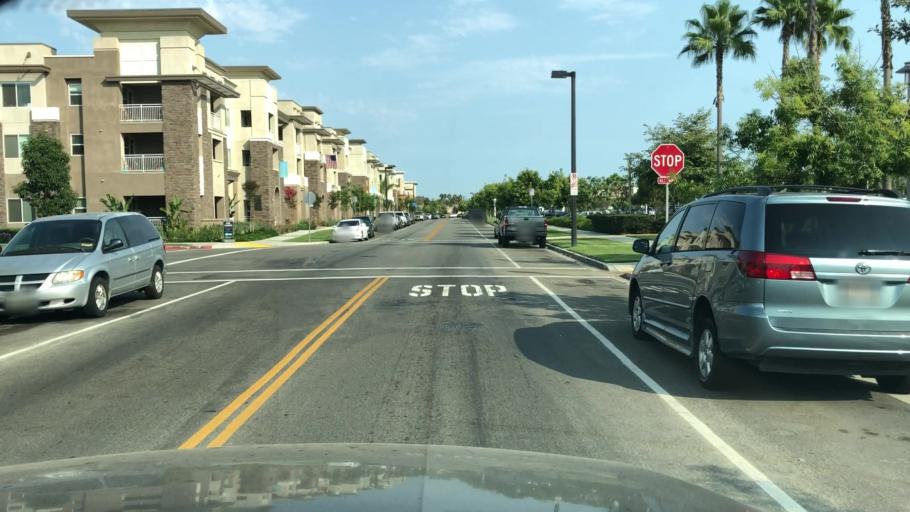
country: US
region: California
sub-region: Ventura County
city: El Rio
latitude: 34.2421
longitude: -119.1759
